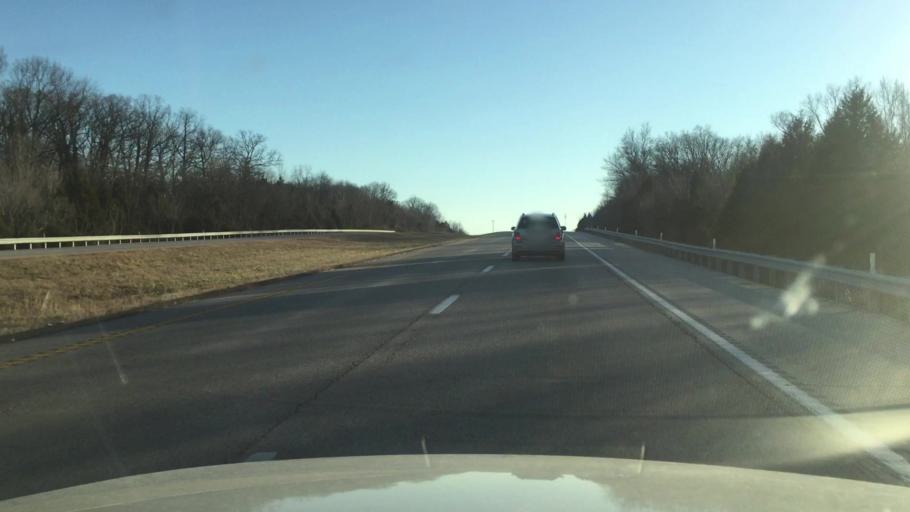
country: US
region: Missouri
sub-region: Cole County
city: Wardsville
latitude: 38.4993
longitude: -92.2677
